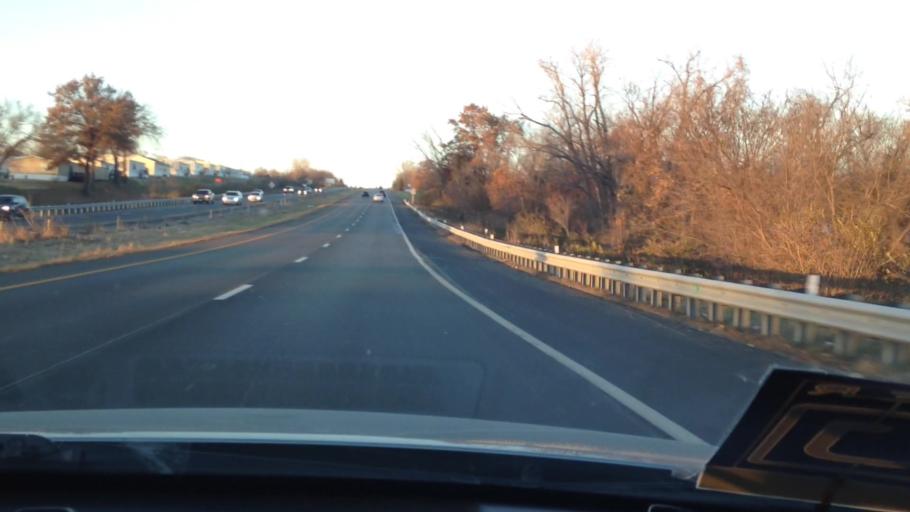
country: US
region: Missouri
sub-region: Platte County
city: Riverside
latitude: 39.1988
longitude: -94.5898
